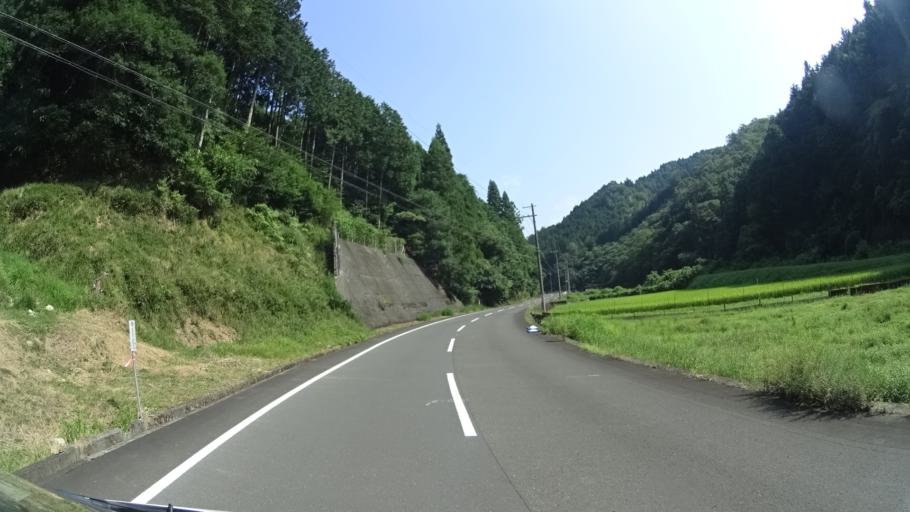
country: JP
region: Kyoto
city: Maizuru
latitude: 35.4198
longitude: 135.2256
